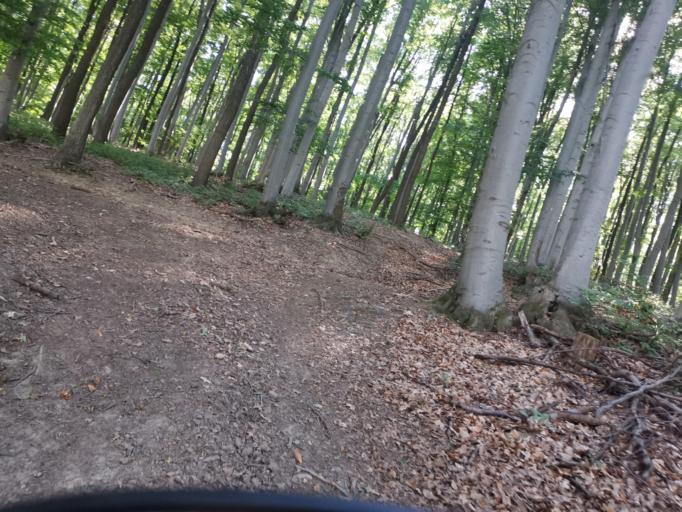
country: CZ
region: South Moravian
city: Knezdub
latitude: 48.7940
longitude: 17.3993
